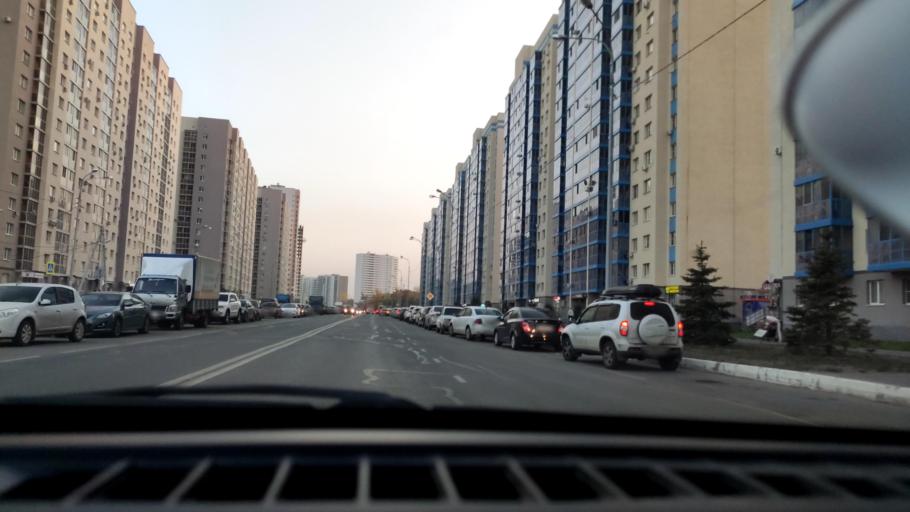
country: RU
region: Samara
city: Rozhdestveno
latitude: 53.1533
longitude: 50.0751
